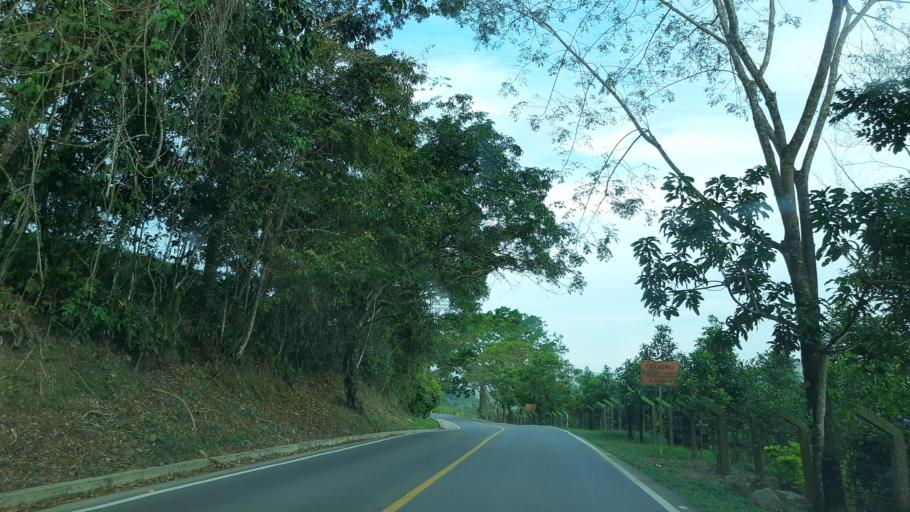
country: CO
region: Boyaca
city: San Luis de Gaceno
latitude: 4.8235
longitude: -73.1995
